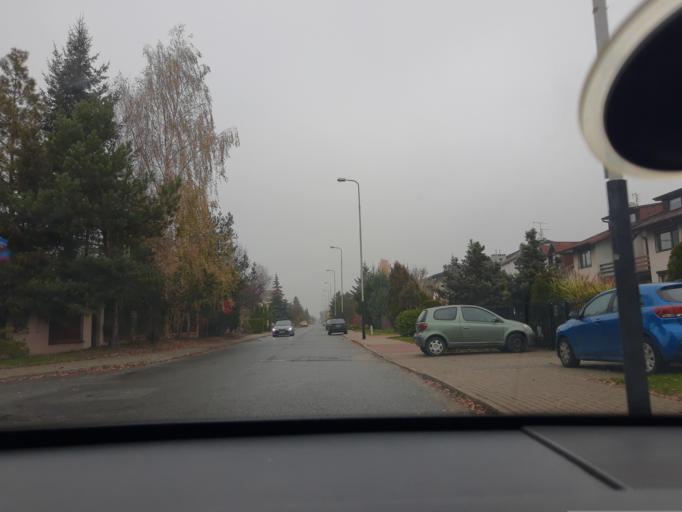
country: PL
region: Lodz Voivodeship
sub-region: Powiat pabianicki
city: Konstantynow Lodzki
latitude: 51.7370
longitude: 19.3805
